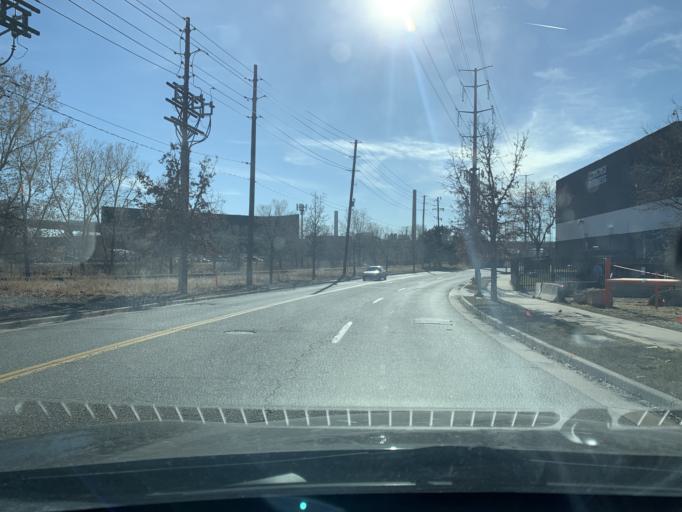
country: US
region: Colorado
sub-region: Denver County
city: Denver
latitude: 39.7431
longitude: -105.0171
